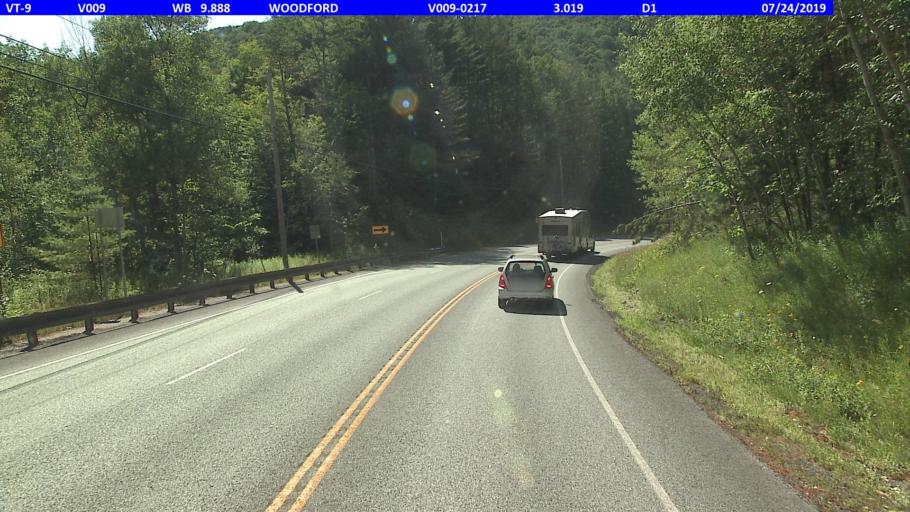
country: US
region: Vermont
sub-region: Bennington County
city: Bennington
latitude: 42.8776
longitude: -73.1158
